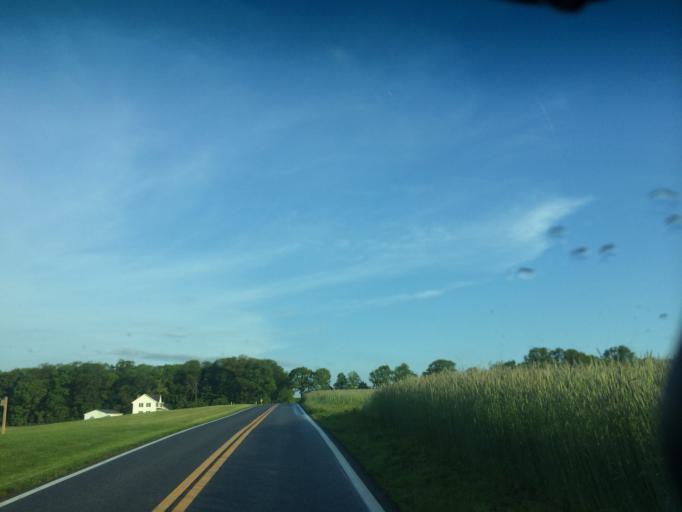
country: US
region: Maryland
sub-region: Carroll County
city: Westminster
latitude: 39.4988
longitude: -77.0115
